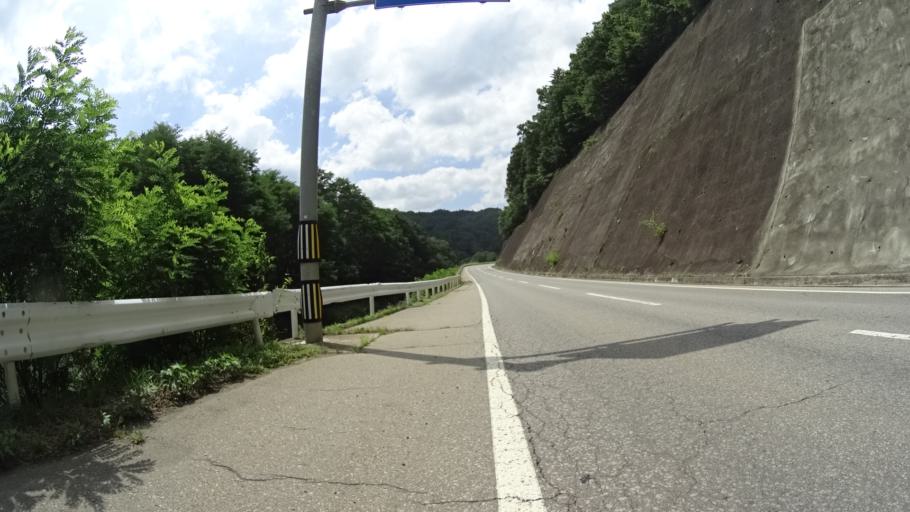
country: JP
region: Nagano
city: Saku
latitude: 36.0603
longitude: 138.5075
